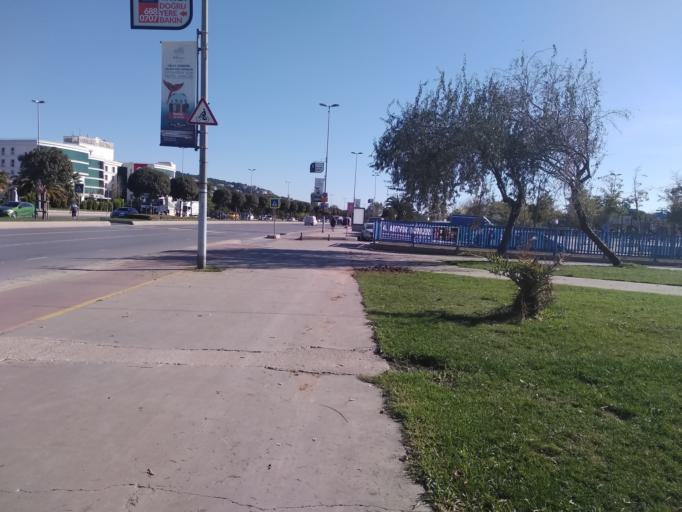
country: TR
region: Istanbul
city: Maltepe
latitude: 40.9160
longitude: 29.1316
